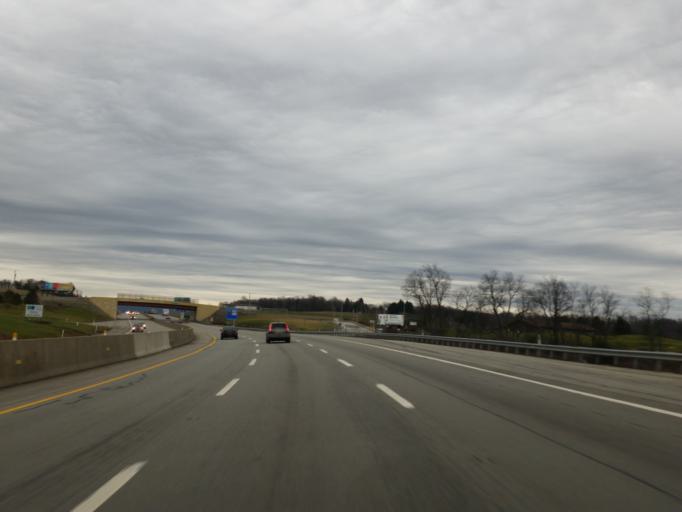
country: US
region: Pennsylvania
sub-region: Fayette County
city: Bear Rocks
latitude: 40.1281
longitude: -79.4073
